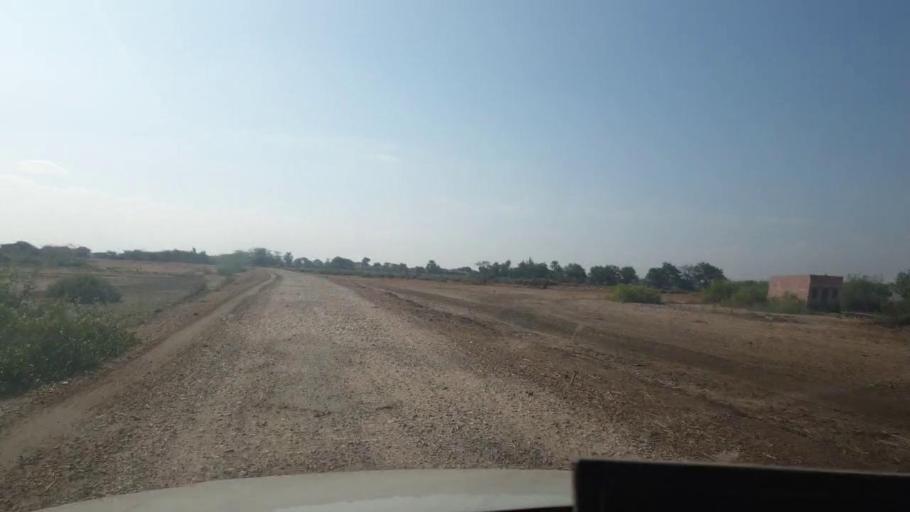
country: PK
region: Sindh
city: Mirpur Sakro
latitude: 24.4697
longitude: 67.5953
